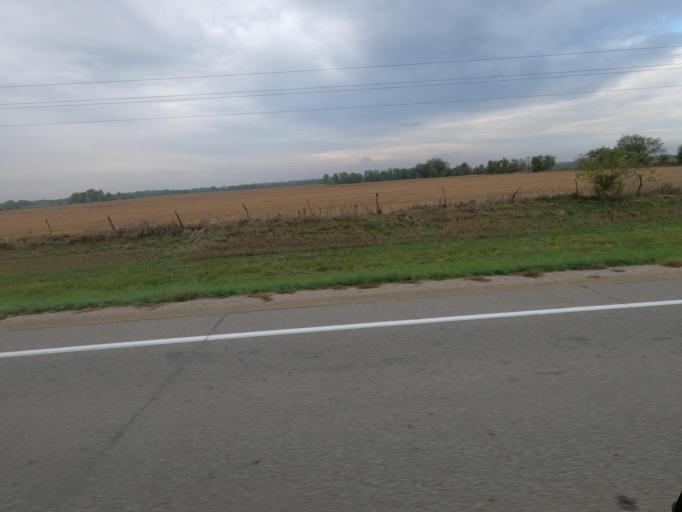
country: US
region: Iowa
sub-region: Henry County
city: Mount Pleasant
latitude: 40.8135
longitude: -91.7147
